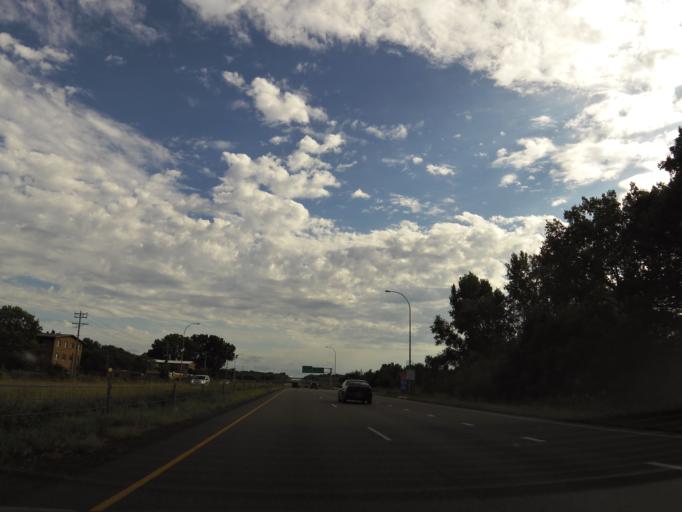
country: US
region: Minnesota
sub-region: Hennepin County
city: New Hope
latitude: 45.0391
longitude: -93.4010
